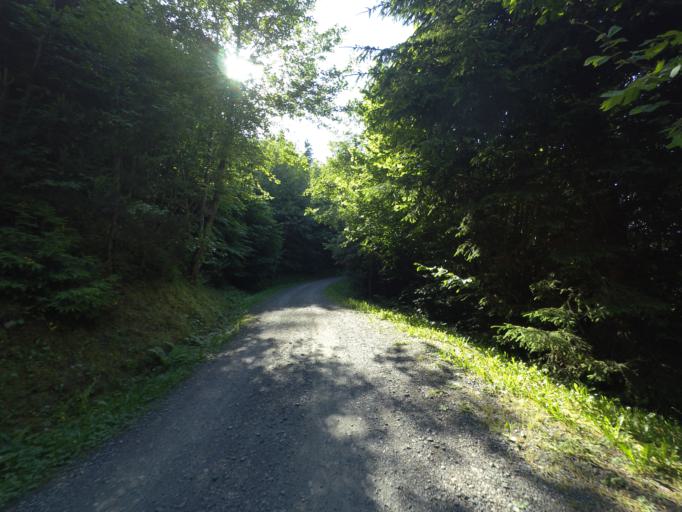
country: AT
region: Carinthia
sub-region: Politischer Bezirk Spittal an der Drau
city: Millstatt
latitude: 46.7993
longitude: 13.5523
